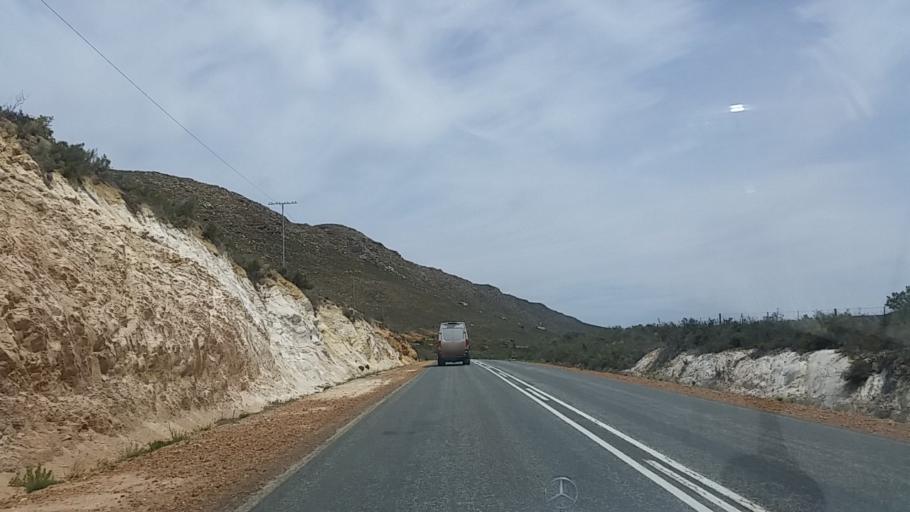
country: ZA
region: Western Cape
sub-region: Eden District Municipality
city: Knysna
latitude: -33.7415
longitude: 23.0338
